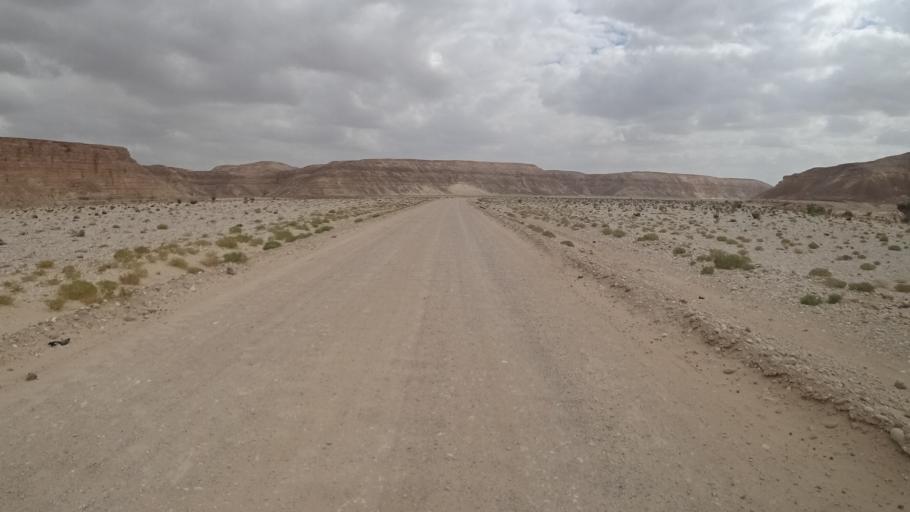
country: YE
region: Al Mahrah
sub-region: Shahan
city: Shihan as Sufla
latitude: 17.4708
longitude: 53.0026
